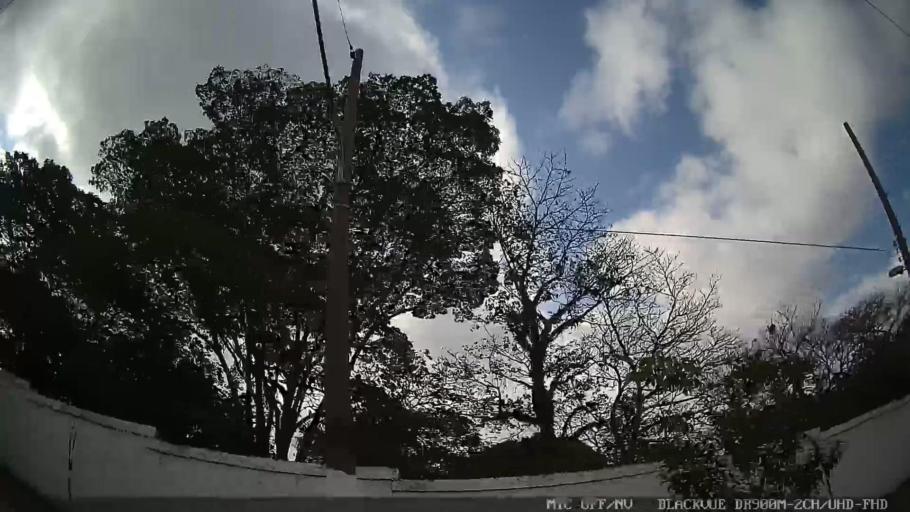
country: BR
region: Sao Paulo
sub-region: Sao Caetano Do Sul
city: Sao Caetano do Sul
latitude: -23.5647
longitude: -46.5240
